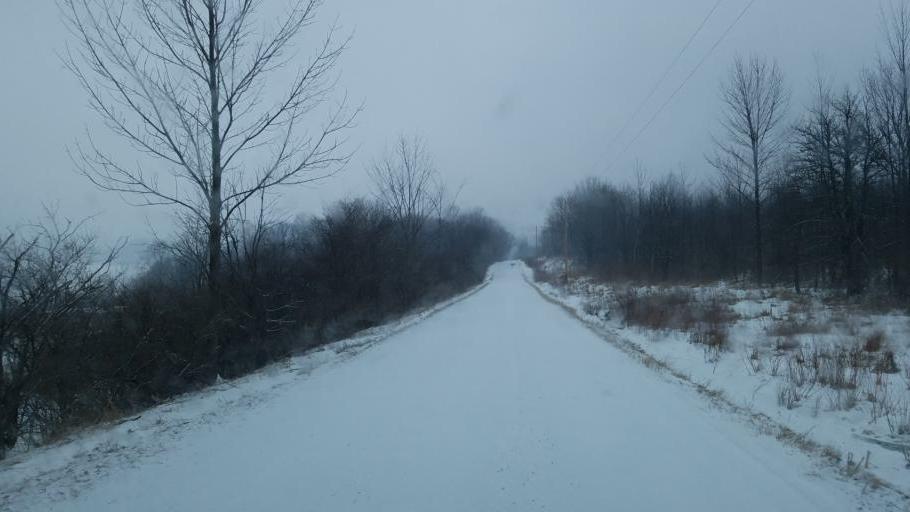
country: US
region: New York
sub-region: Steuben County
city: Canisteo
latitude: 42.1262
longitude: -77.5445
